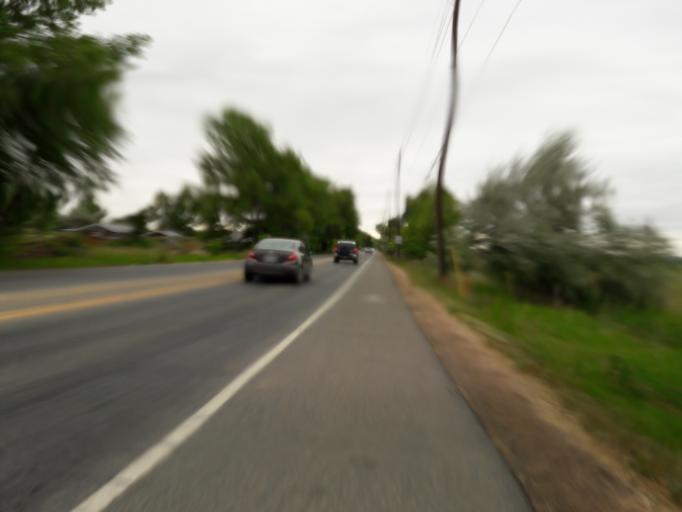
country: US
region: Colorado
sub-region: Boulder County
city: Boulder
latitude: 40.0510
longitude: -105.2319
